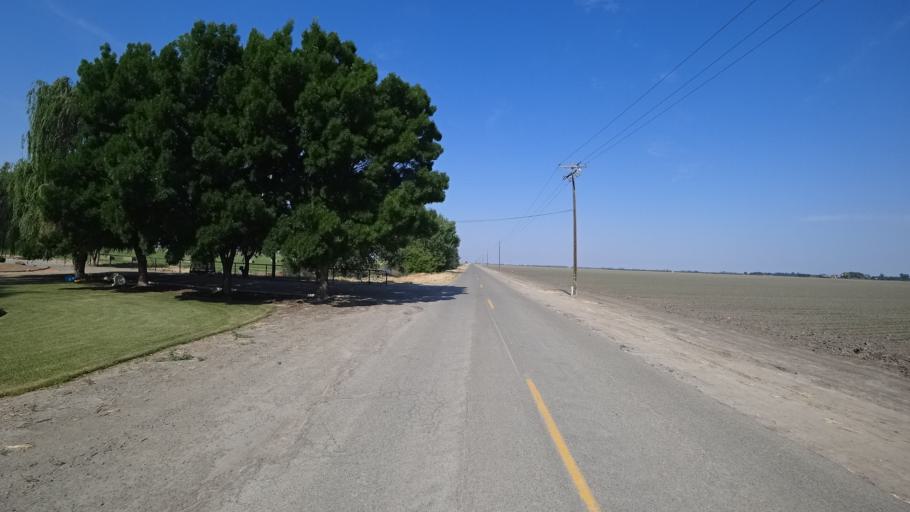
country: US
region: California
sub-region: Kings County
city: Lemoore
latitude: 36.3134
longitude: -119.8343
